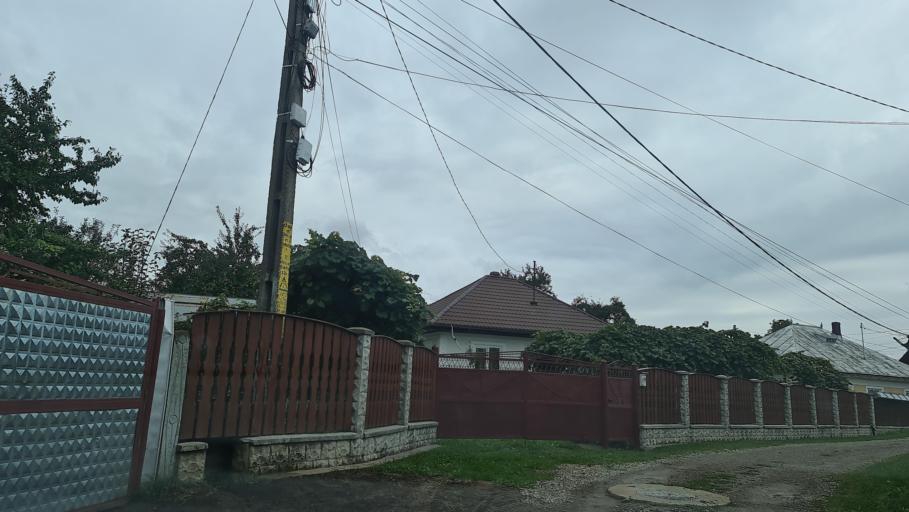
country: RO
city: Vanatori-Neamt
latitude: 47.2084
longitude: 26.3129
